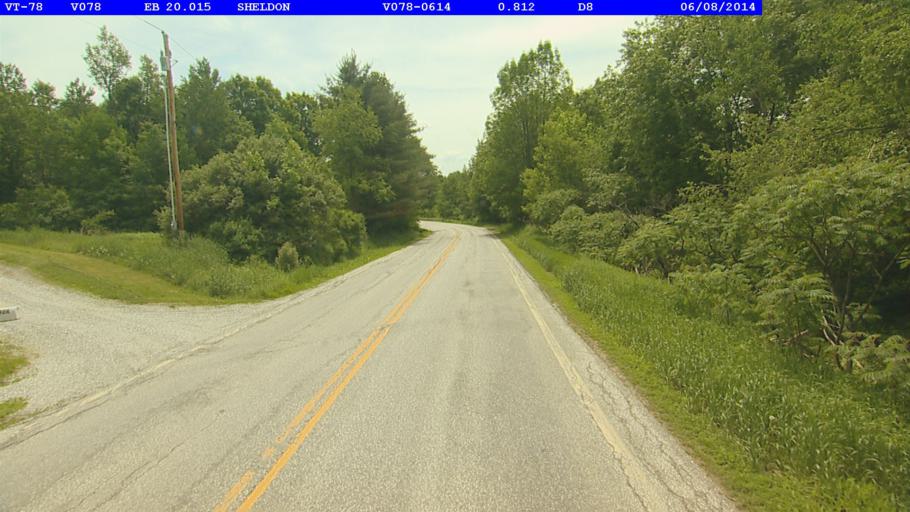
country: US
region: Vermont
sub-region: Franklin County
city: Enosburg Falls
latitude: 44.9150
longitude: -72.9586
